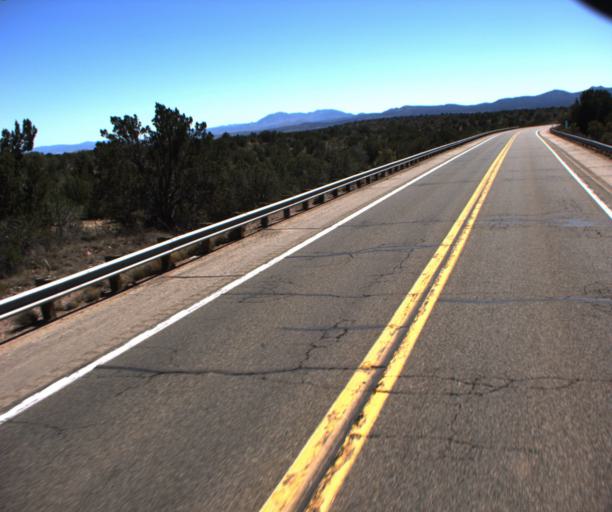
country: US
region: Arizona
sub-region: Yavapai County
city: Paulden
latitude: 34.9349
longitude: -112.4350
